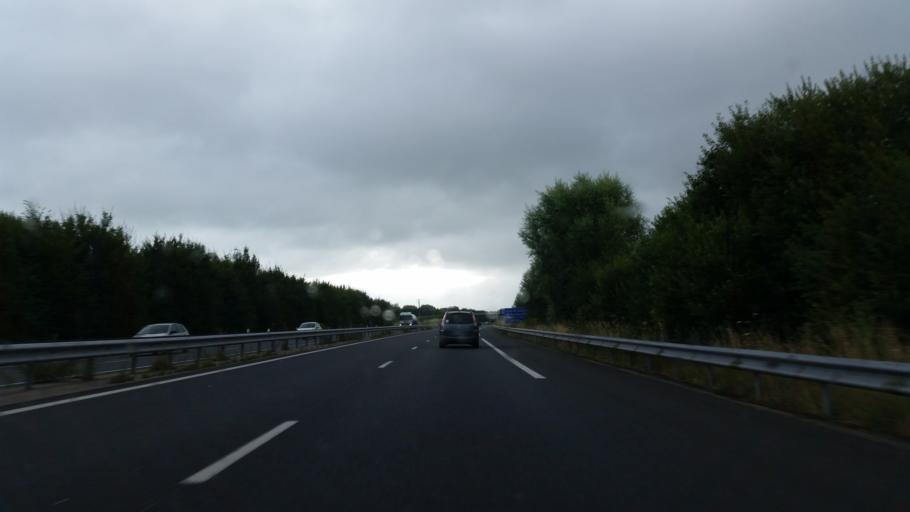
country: FR
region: Haute-Normandie
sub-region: Departement de l'Eure
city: Beuzeville
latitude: 49.3252
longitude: 0.2967
